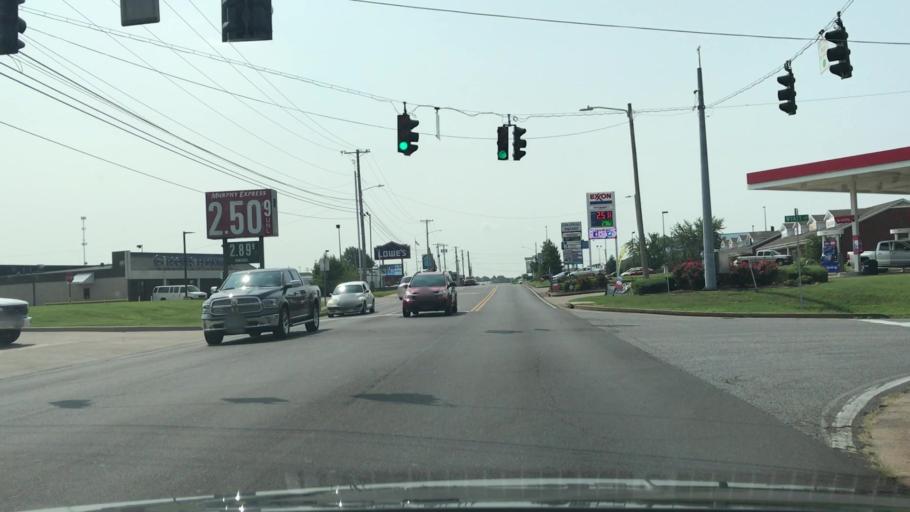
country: US
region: Kentucky
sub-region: Graves County
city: Mayfield
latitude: 36.7227
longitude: -88.6274
